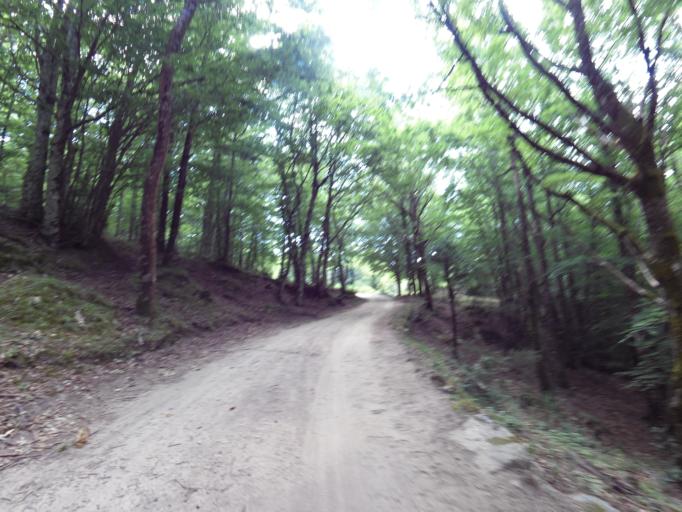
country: IT
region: Calabria
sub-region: Provincia di Vibo-Valentia
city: Nardodipace
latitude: 38.5094
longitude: 16.3826
